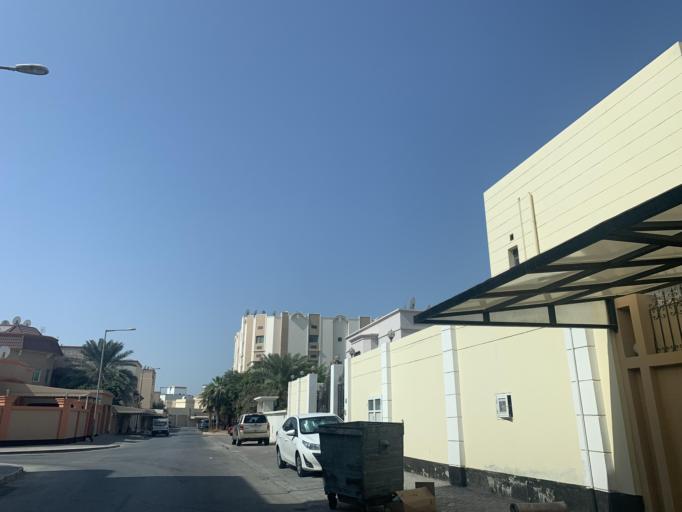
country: BH
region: Central Governorate
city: Madinat Hamad
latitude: 26.1379
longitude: 50.4947
